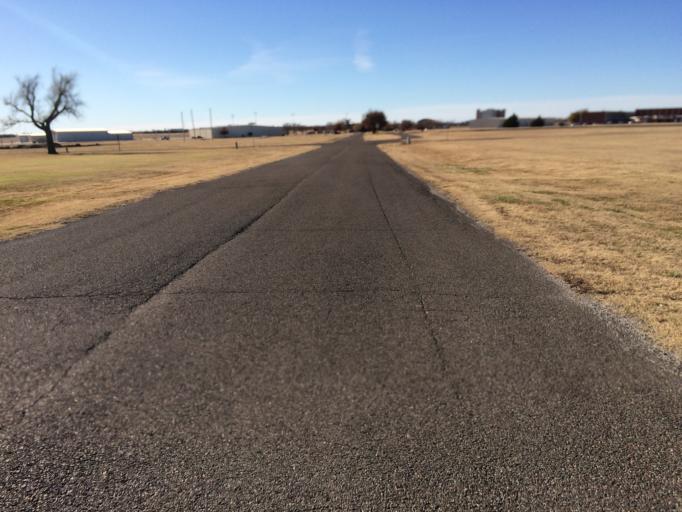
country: US
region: Oklahoma
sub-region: Cleveland County
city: Norman
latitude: 35.2409
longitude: -97.4621
